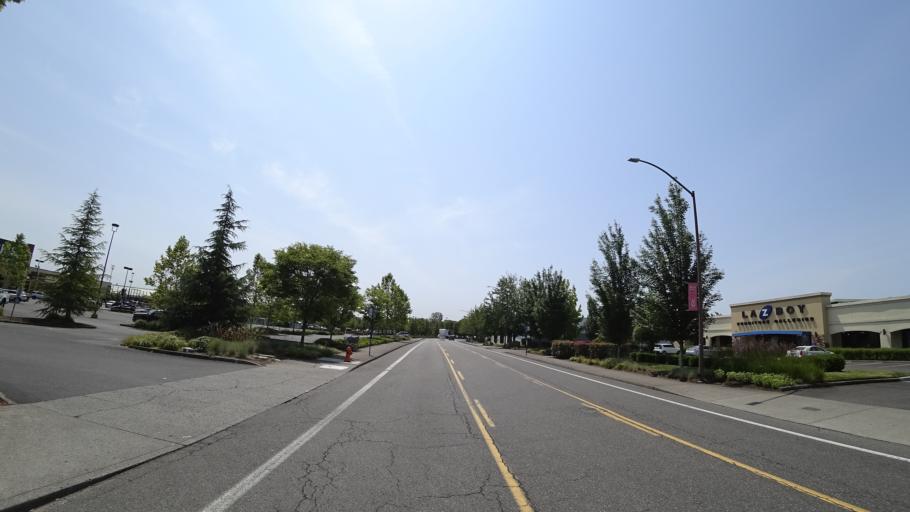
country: US
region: Washington
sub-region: Clark County
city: Vancouver
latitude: 45.5949
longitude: -122.6786
